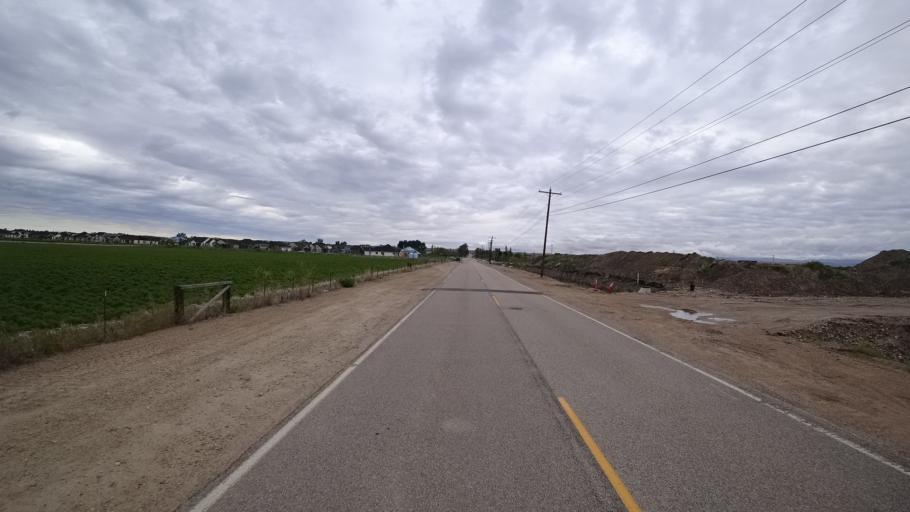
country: US
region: Idaho
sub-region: Ada County
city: Star
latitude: 43.7008
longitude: -116.4435
